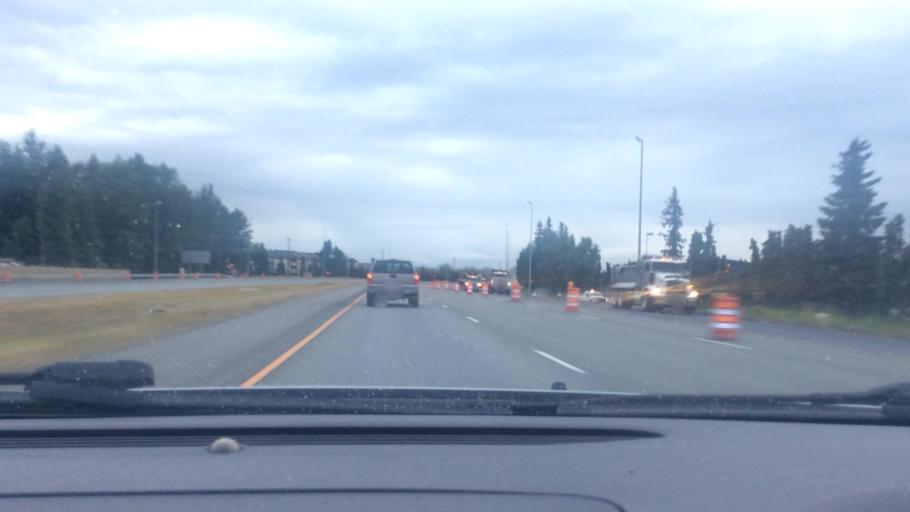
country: US
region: Alaska
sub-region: Anchorage Municipality
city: Elmendorf Air Force Base
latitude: 61.2256
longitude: -149.7411
